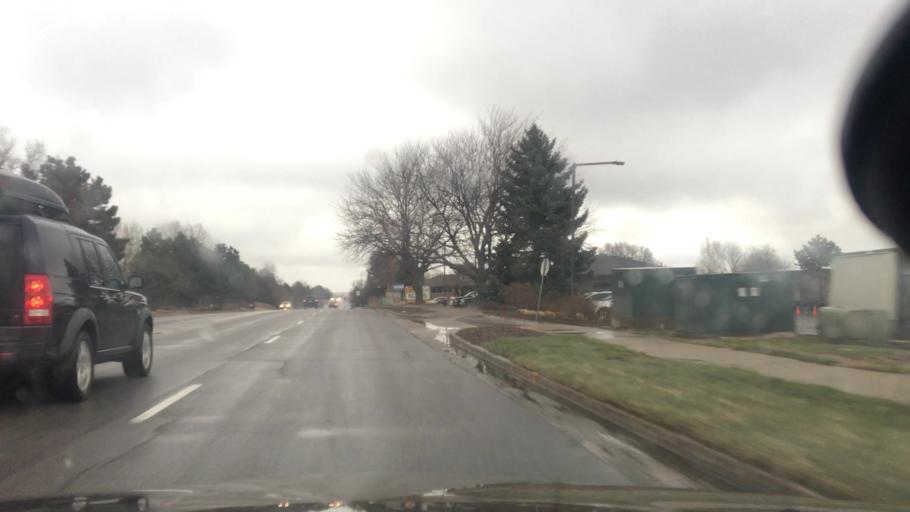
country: US
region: Colorado
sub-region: Arapahoe County
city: Castlewood
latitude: 39.5714
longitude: -104.9230
